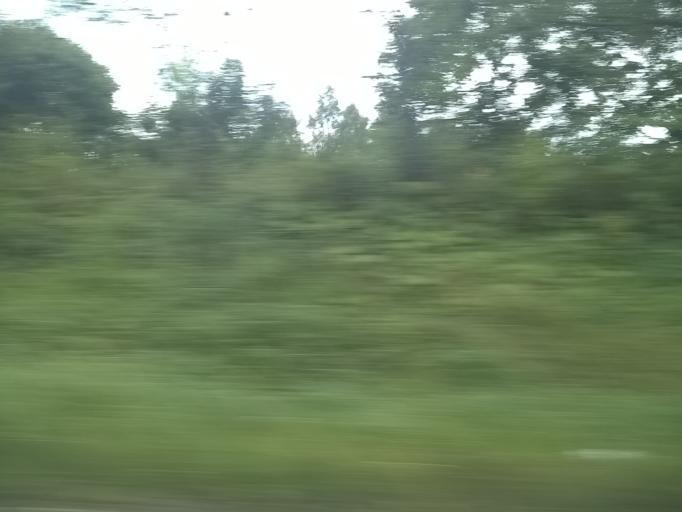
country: FI
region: Pirkanmaa
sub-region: Tampere
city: Tampere
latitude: 61.4981
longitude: 23.8128
